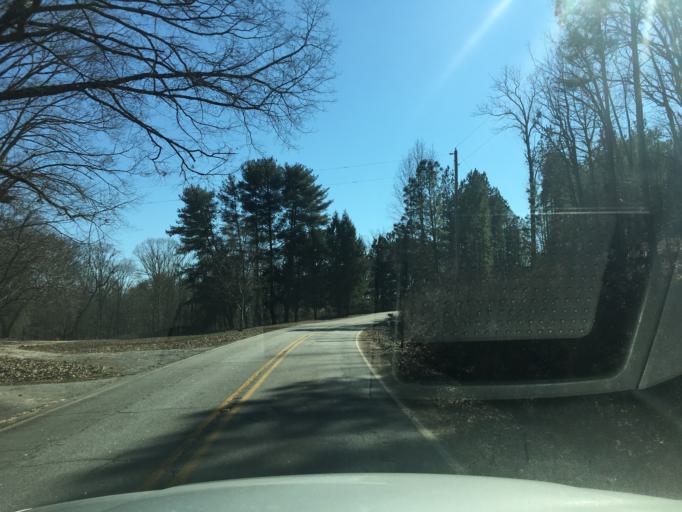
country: US
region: South Carolina
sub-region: Pickens County
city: Pickens
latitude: 34.8332
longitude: -82.7879
